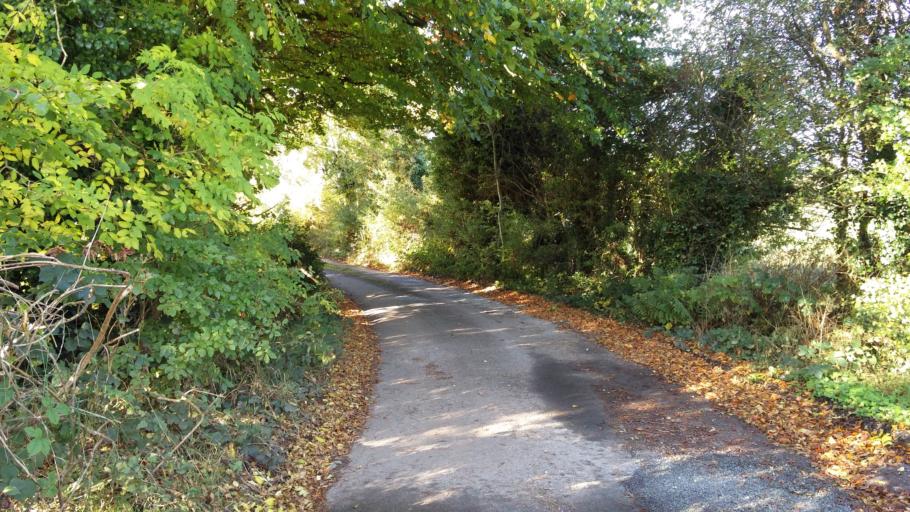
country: IE
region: Connaught
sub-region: Maigh Eo
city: Westport
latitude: 53.7805
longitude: -9.4466
